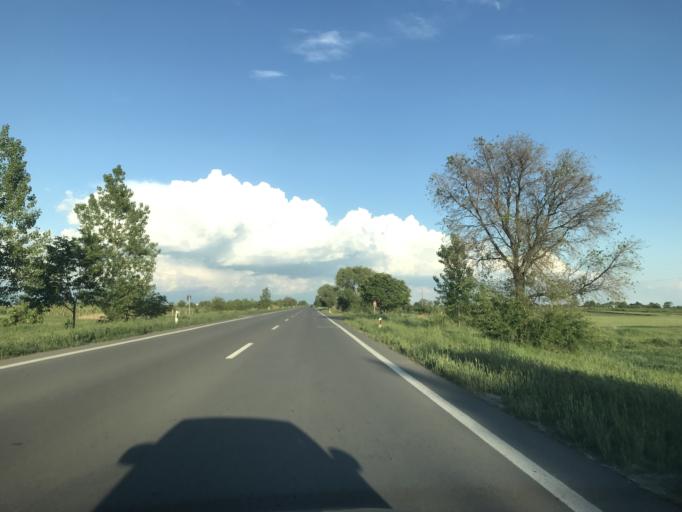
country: RS
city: Aradac
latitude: 45.3905
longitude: 20.3037
